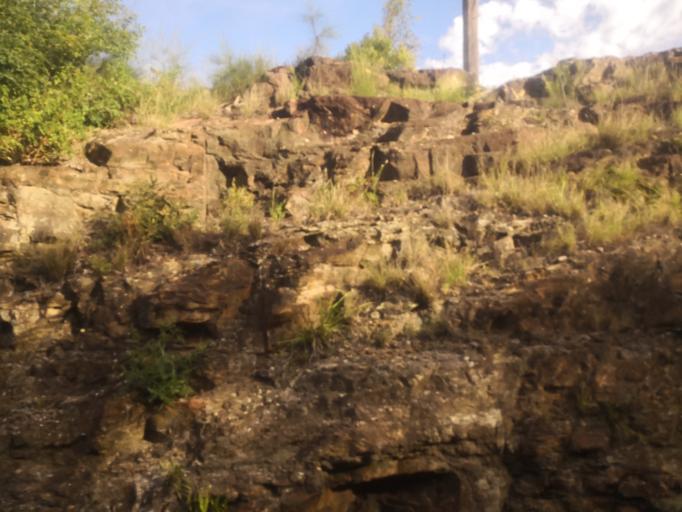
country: AU
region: New South Wales
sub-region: Gosford Shire
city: Point Clare
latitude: -33.4503
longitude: 151.3199
